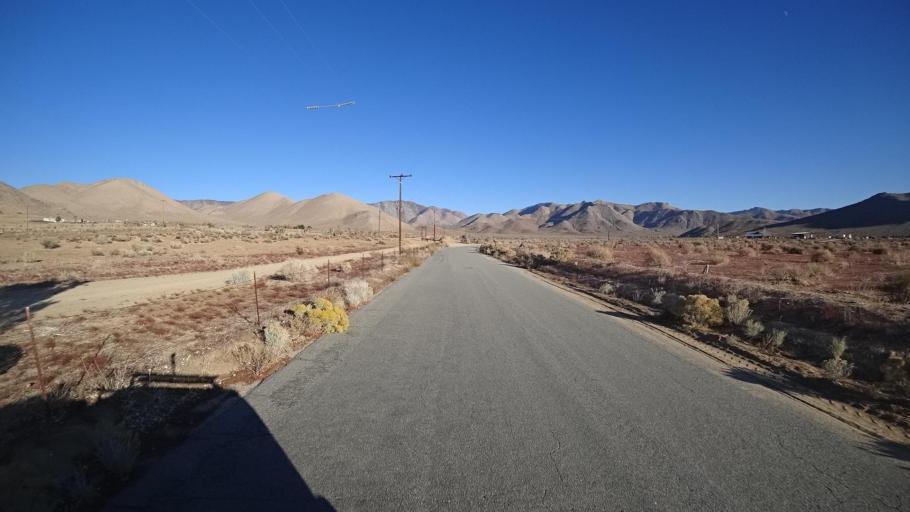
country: US
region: California
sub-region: Kern County
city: Weldon
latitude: 35.5585
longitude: -118.2313
